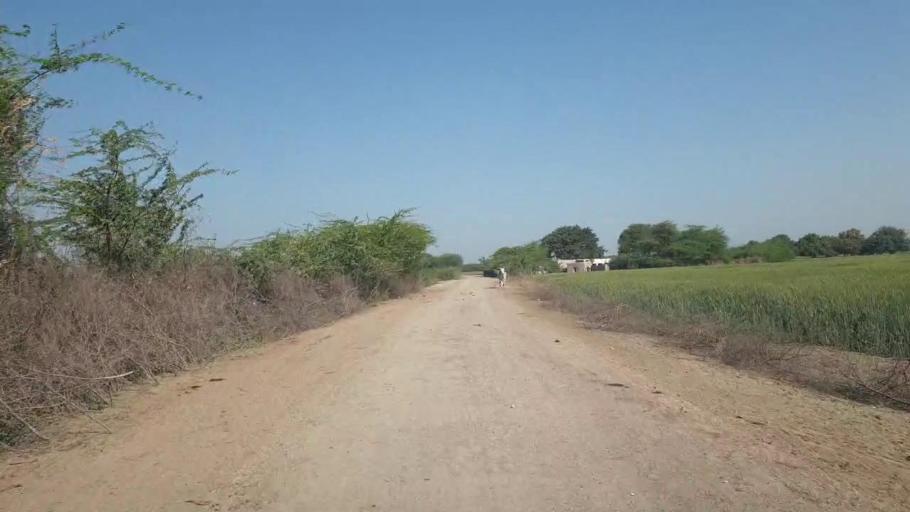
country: PK
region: Sindh
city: Umarkot
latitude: 25.2984
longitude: 69.6546
